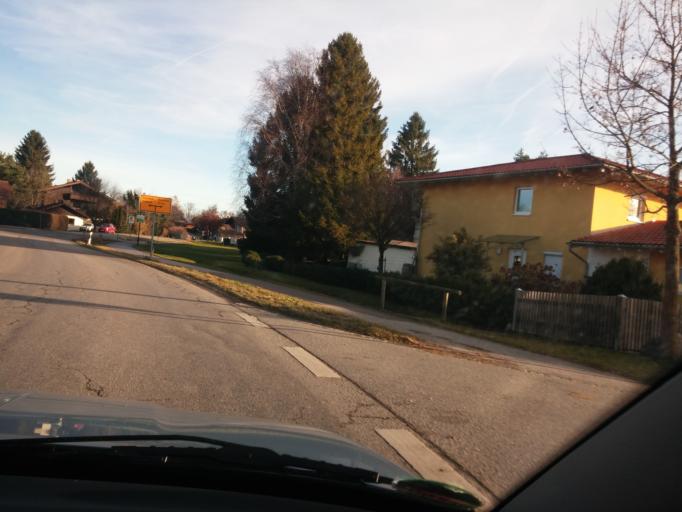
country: DE
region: Bavaria
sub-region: Upper Bavaria
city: Seeon-Seebruck
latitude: 47.9369
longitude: 12.4720
